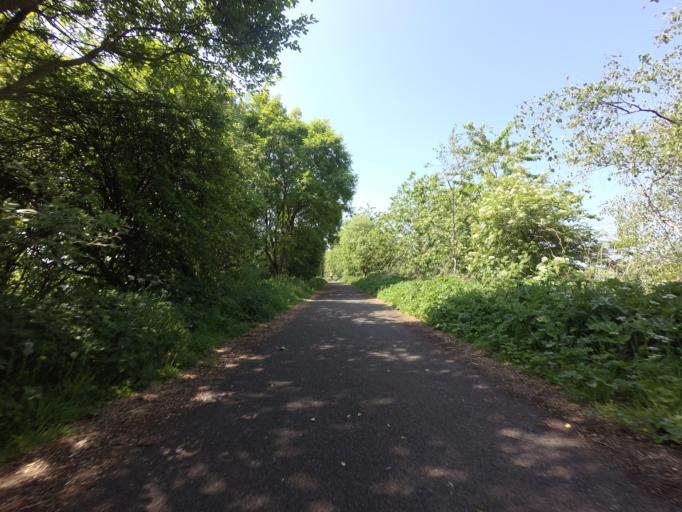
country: GB
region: Scotland
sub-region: Fife
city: Townhill
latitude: 56.0926
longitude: -3.4441
